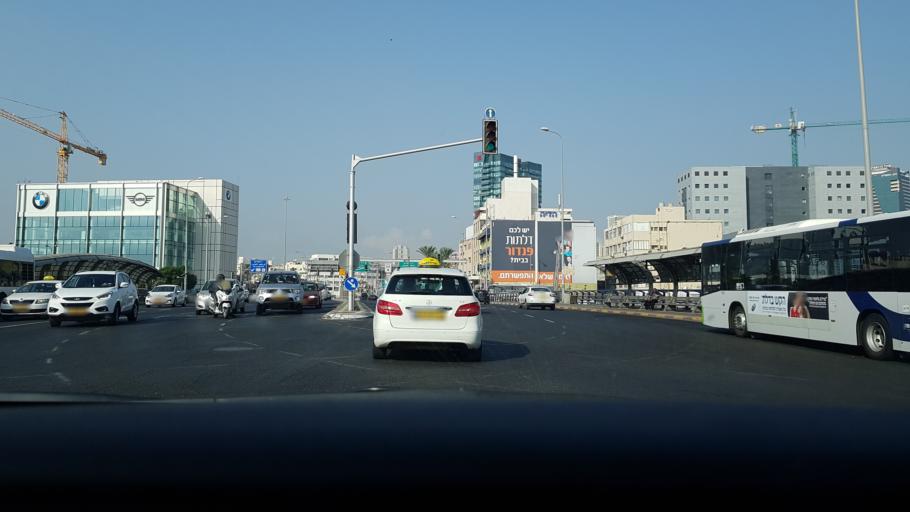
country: IL
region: Tel Aviv
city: Tel Aviv
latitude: 32.0594
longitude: 34.7870
